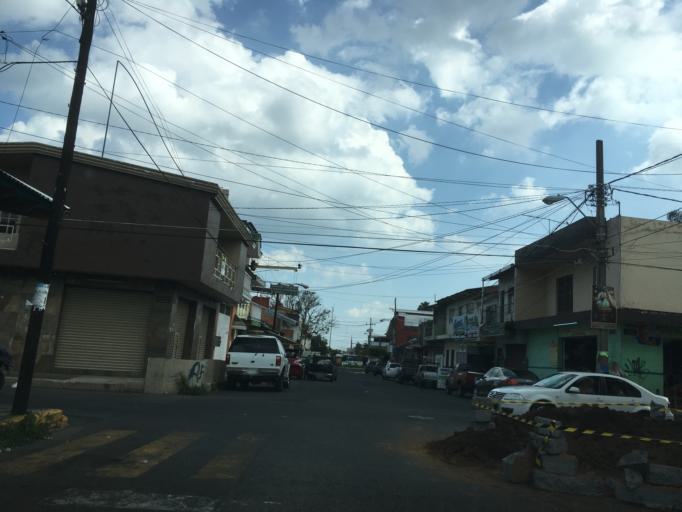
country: MX
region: Michoacan
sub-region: Uruapan
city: Uruapan
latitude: 19.4211
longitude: -102.0519
